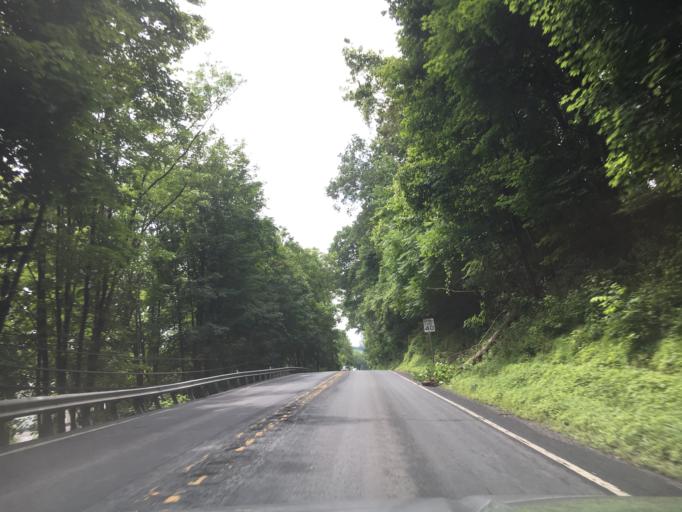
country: US
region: Pennsylvania
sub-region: Lehigh County
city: Laurys Station
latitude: 40.7176
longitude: -75.5259
